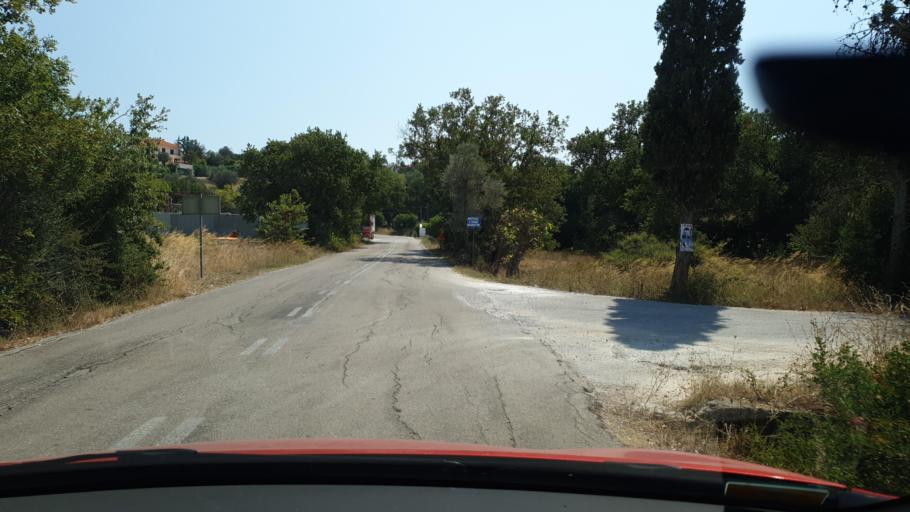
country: GR
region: Central Greece
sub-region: Nomos Evvoias
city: Oxilithos
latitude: 38.5382
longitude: 24.0778
